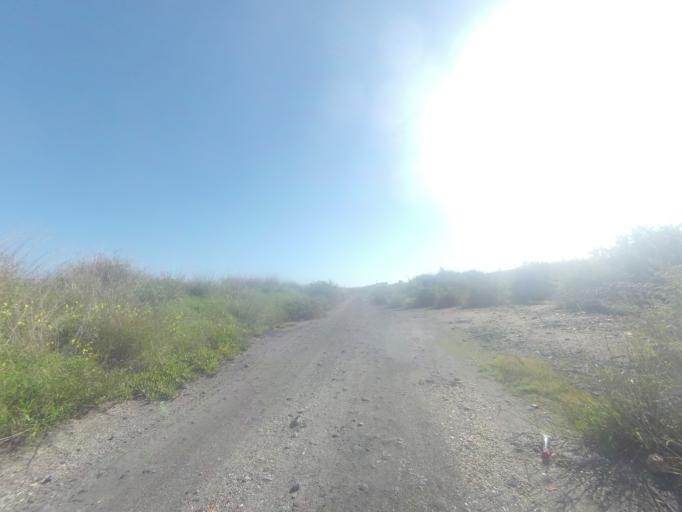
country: ES
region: Andalusia
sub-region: Provincia de Huelva
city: Palos de la Frontera
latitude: 37.2528
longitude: -6.9053
